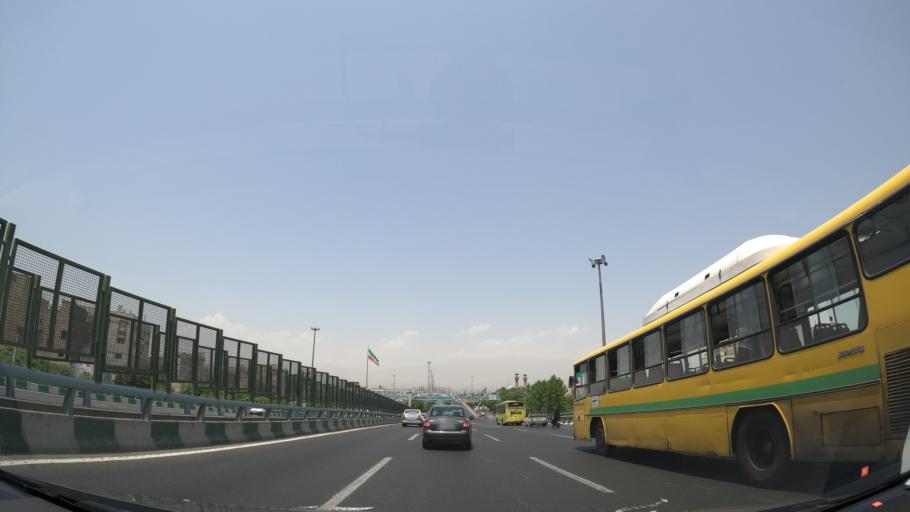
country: IR
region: Tehran
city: Tehran
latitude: 35.6605
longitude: 51.3822
